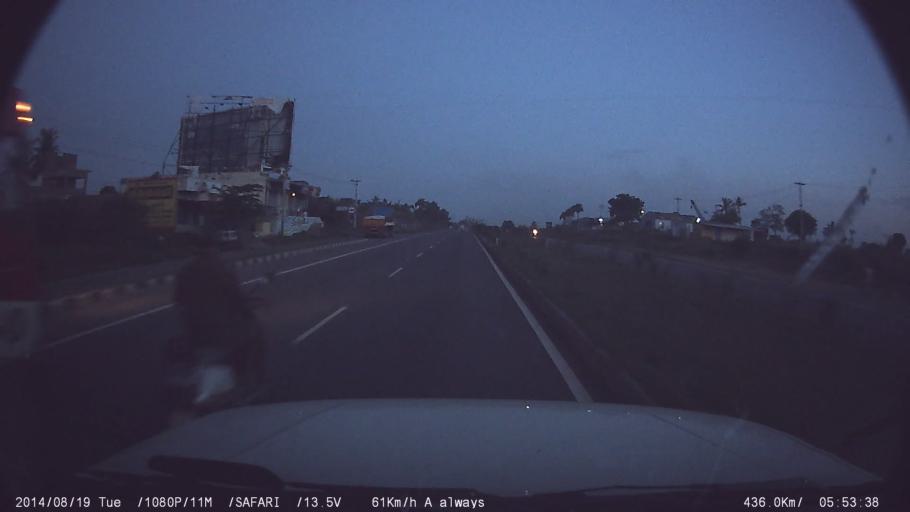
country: IN
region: Tamil Nadu
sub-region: Salem
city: Omalur
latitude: 11.7251
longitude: 78.0670
